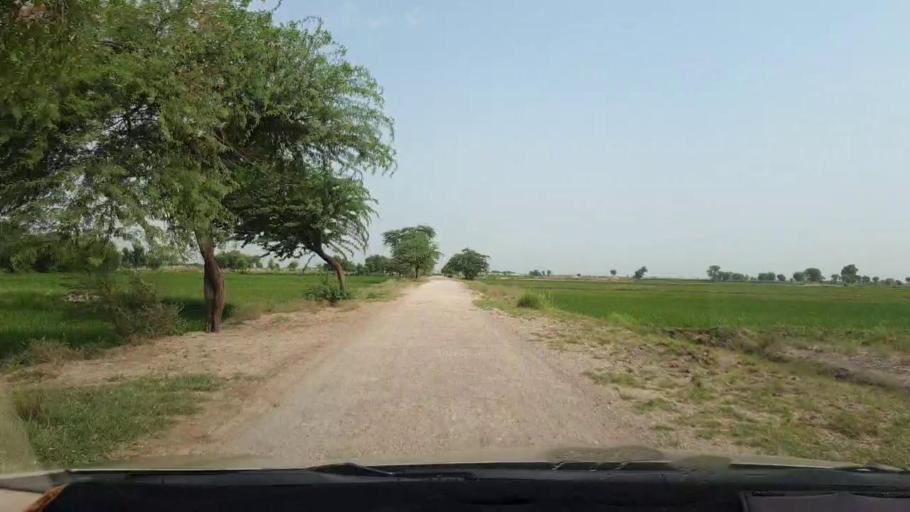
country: PK
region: Sindh
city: Larkana
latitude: 27.6786
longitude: 68.2196
